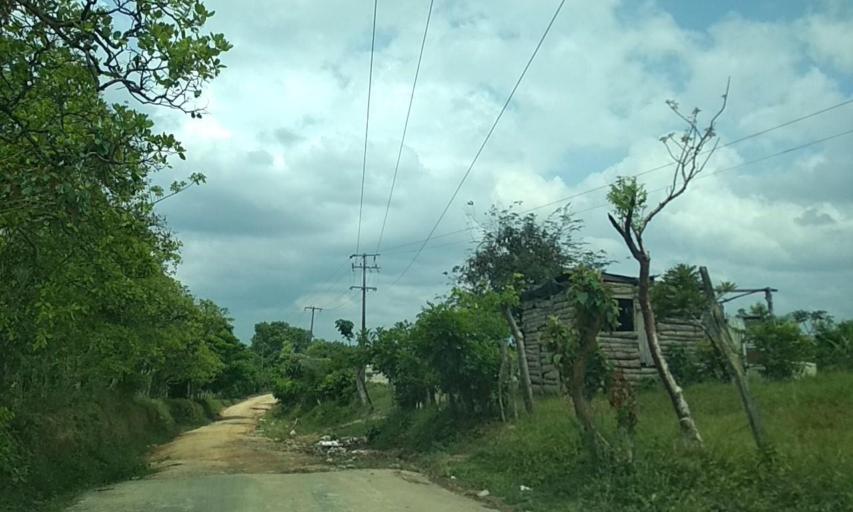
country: MX
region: Veracruz
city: Las Choapas
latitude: 17.8887
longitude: -94.1121
